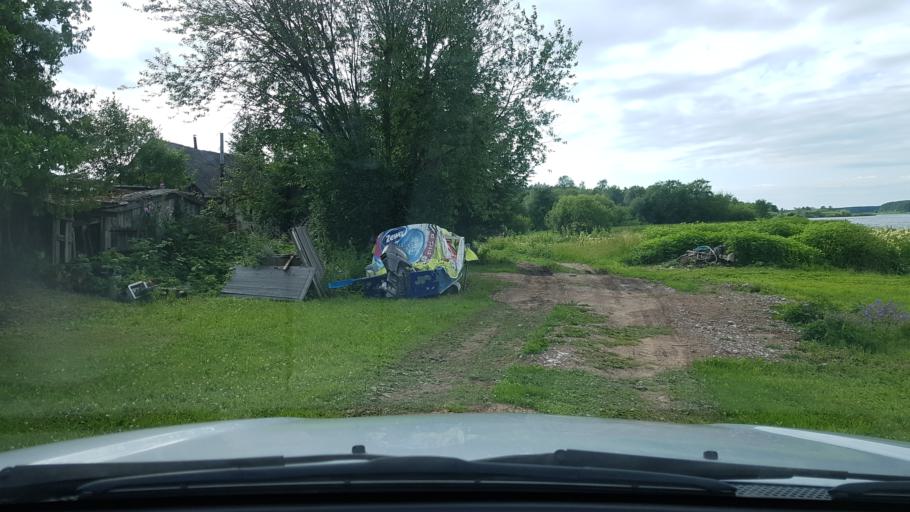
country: EE
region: Ida-Virumaa
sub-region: Narva-Joesuu linn
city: Narva-Joesuu
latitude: 59.4518
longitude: 28.0849
